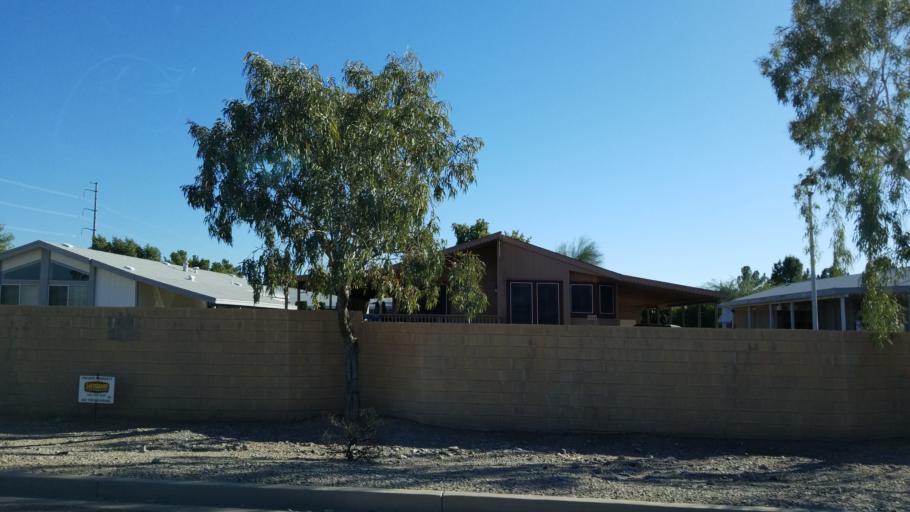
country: US
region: Arizona
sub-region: Maricopa County
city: Cave Creek
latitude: 33.6987
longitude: -111.9976
